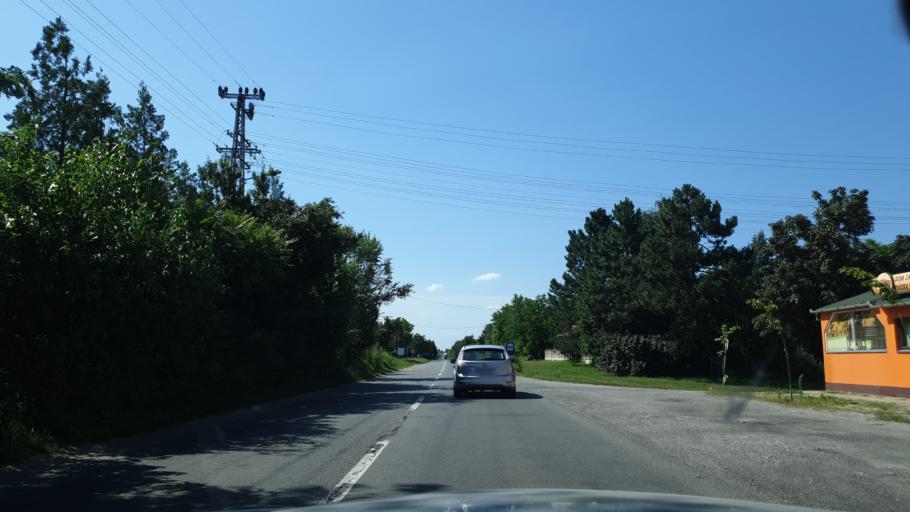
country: HU
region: Bacs-Kiskun
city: Kelebia
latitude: 46.1517
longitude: 19.5788
